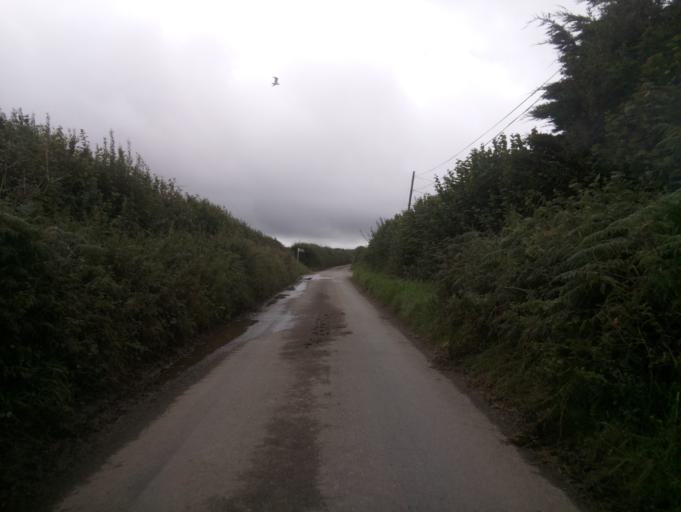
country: GB
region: England
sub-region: Devon
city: Kingsbridge
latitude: 50.3069
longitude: -3.7167
